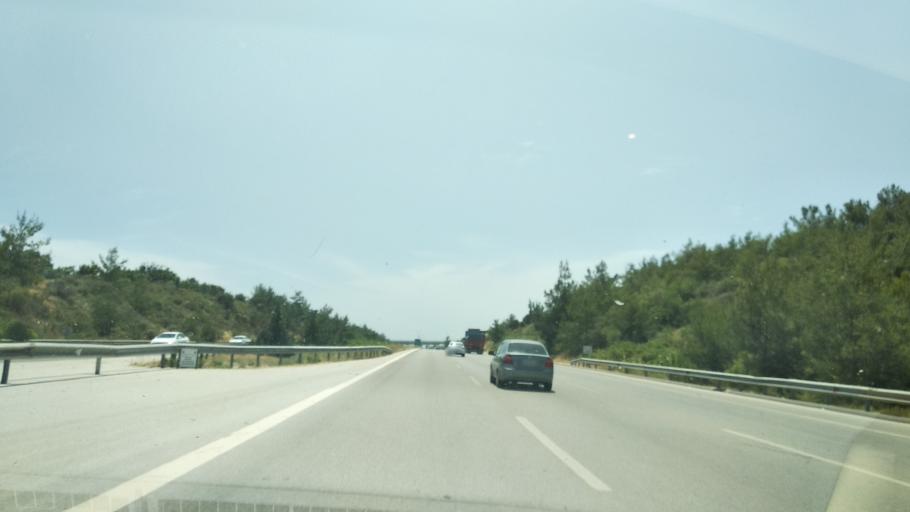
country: TR
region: Mersin
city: Mezitli
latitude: 36.7774
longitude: 34.4887
